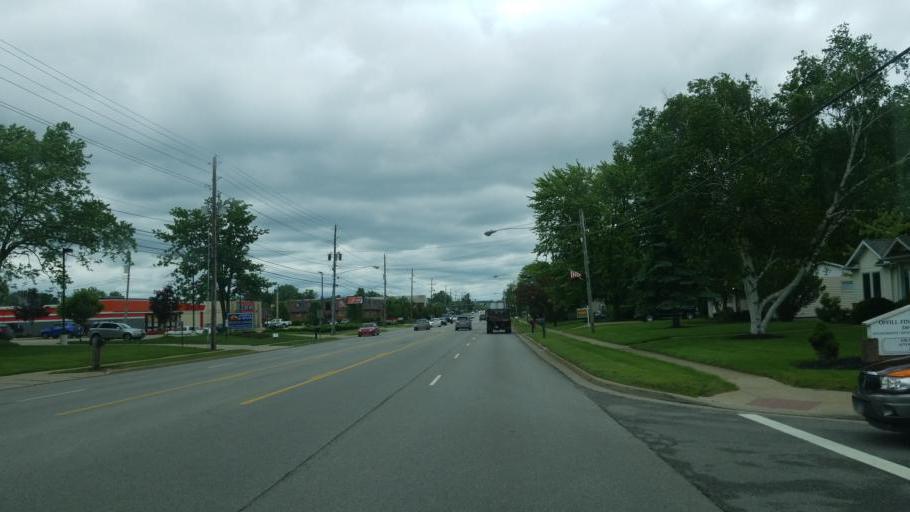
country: US
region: Ohio
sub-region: Medina County
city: Brunswick
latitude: 41.2382
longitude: -81.8367
